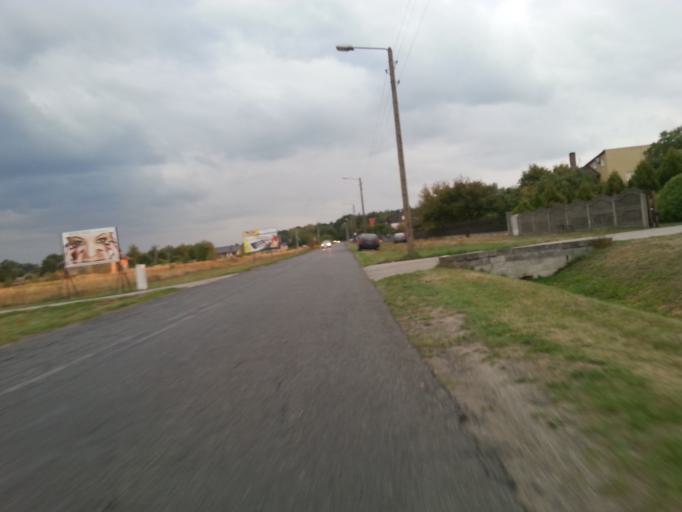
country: PL
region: Lower Silesian Voivodeship
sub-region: Powiat olesnicki
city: Twardogora
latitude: 51.3545
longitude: 17.4537
